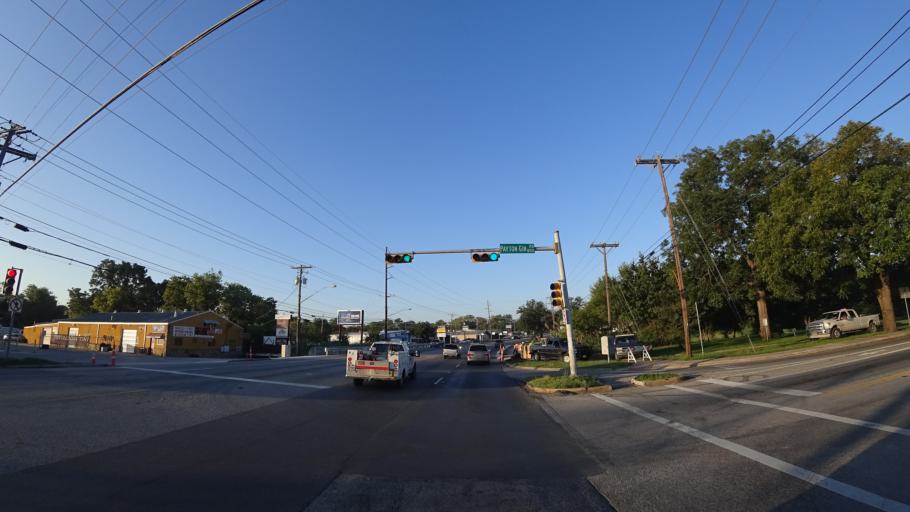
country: US
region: Texas
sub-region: Travis County
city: Wells Branch
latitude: 30.3577
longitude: -97.7002
